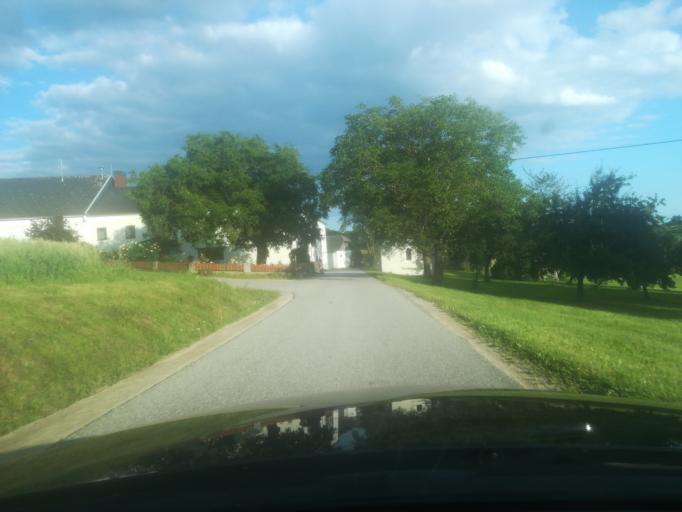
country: AT
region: Upper Austria
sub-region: Politischer Bezirk Perg
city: Perg
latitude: 48.3592
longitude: 14.5705
